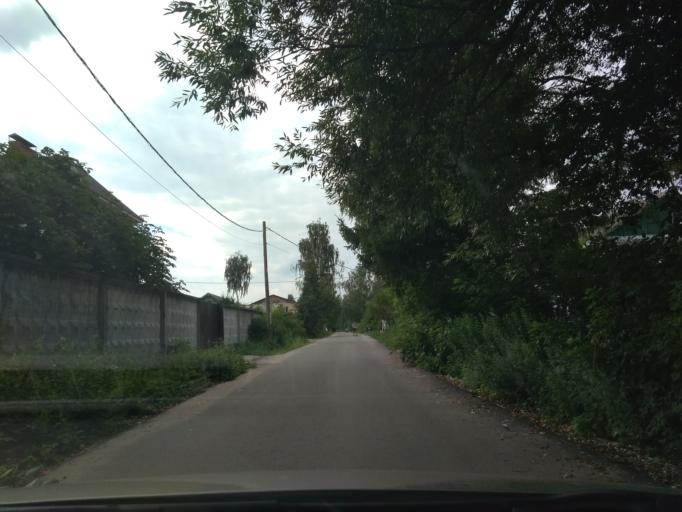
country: RU
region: Moskovskaya
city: Kabanovo
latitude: 55.7863
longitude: 38.9240
